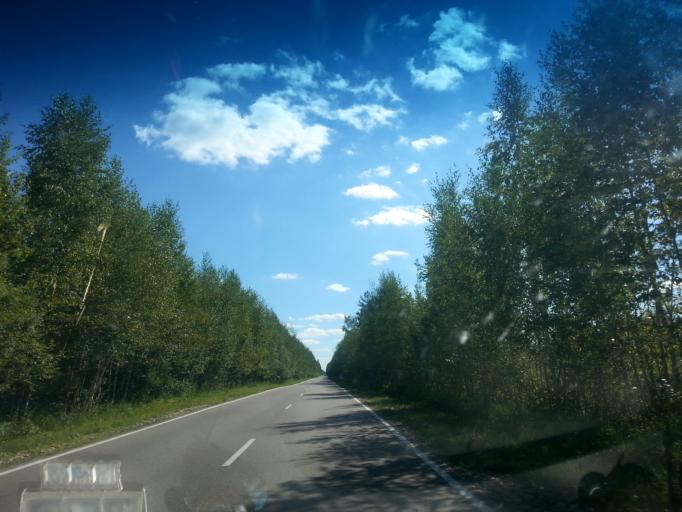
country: RU
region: Vladimir
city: Galitsy
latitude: 56.1302
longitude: 42.8738
